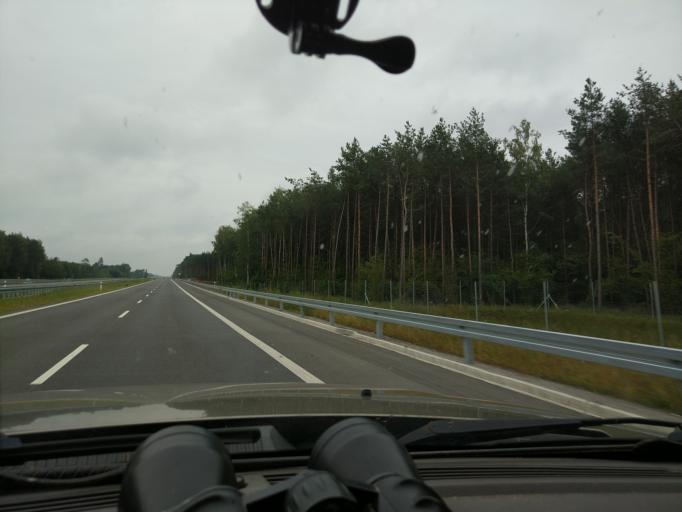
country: PL
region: Masovian Voivodeship
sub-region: Powiat ostrowski
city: Ostrow Mazowiecka
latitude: 52.8338
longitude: 21.9502
